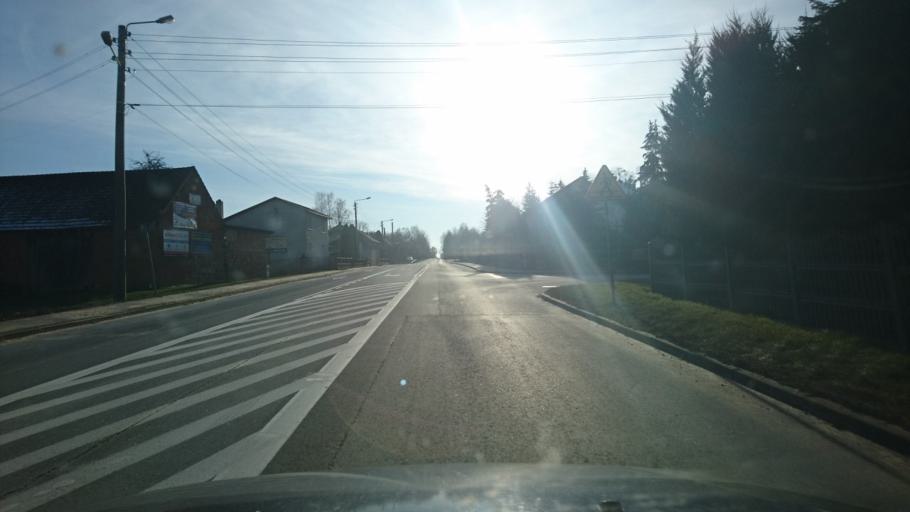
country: PL
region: Opole Voivodeship
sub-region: Powiat oleski
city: Dalachow
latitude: 51.0761
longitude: 18.6027
